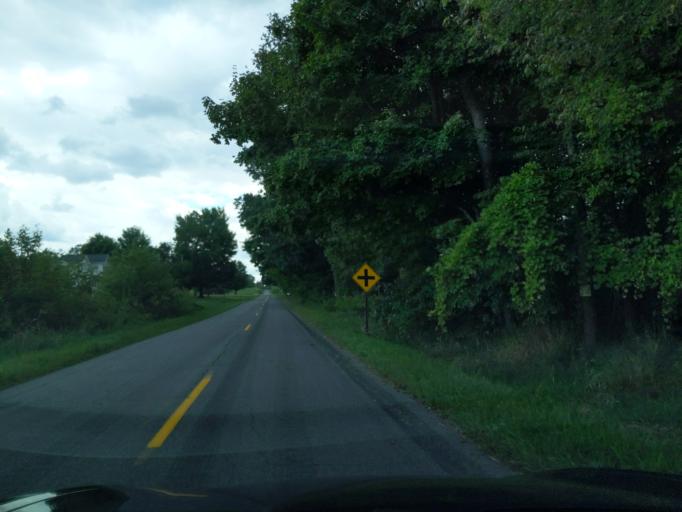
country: US
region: Michigan
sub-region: Eaton County
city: Eaton Rapids
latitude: 42.4103
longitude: -84.5809
